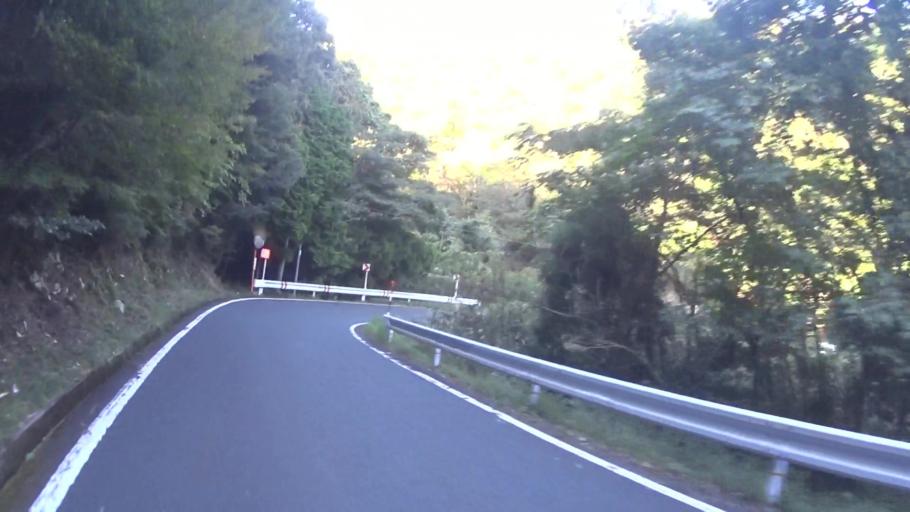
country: JP
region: Hyogo
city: Toyooka
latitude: 35.6121
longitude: 134.8839
